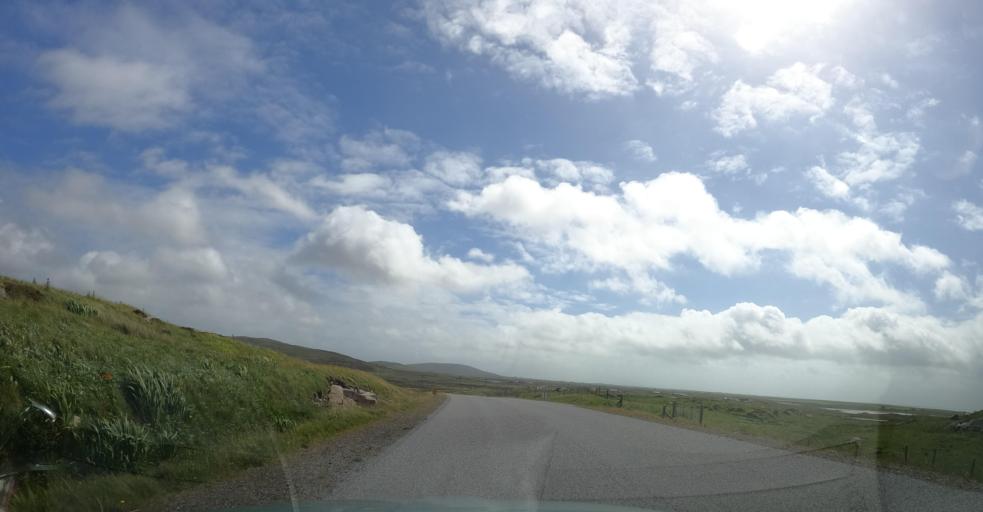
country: GB
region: Scotland
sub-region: Eilean Siar
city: Isle of South Uist
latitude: 57.2320
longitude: -7.3978
